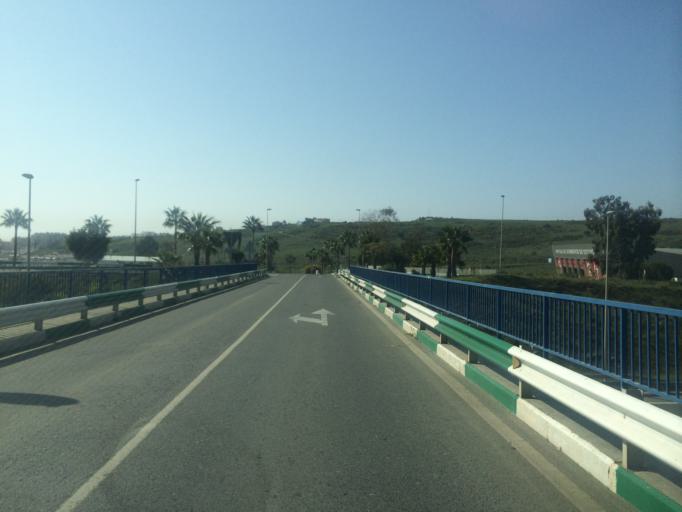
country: ES
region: Andalusia
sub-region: Provincia de Malaga
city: Estepona
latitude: 36.4335
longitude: -5.1614
